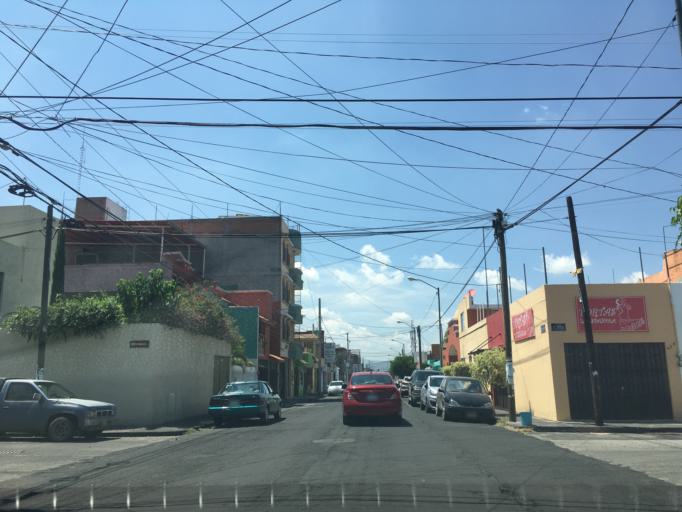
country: MX
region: Michoacan
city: Morelia
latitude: 19.6899
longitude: -101.1825
